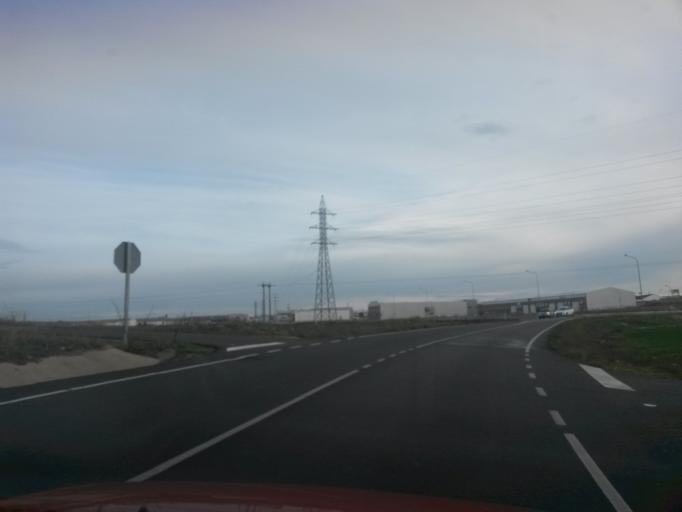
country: ES
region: Castille and Leon
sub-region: Provincia de Salamanca
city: Villares de la Reina
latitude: 40.9995
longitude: -5.6399
